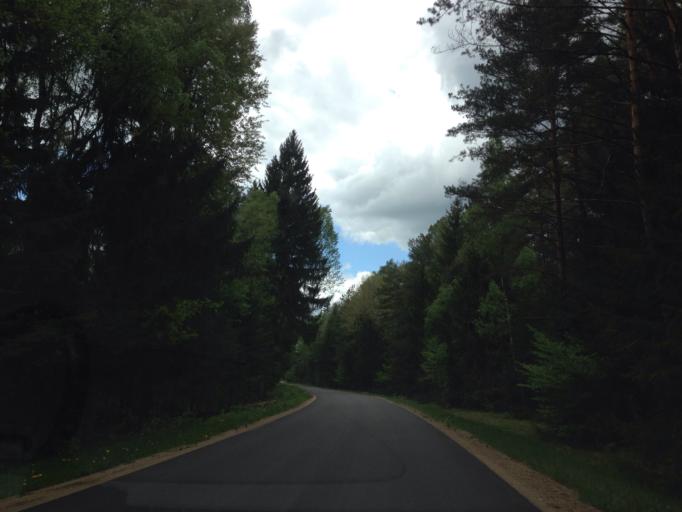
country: PL
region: Podlasie
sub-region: Powiat moniecki
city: Goniadz
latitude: 53.3618
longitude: 22.5993
